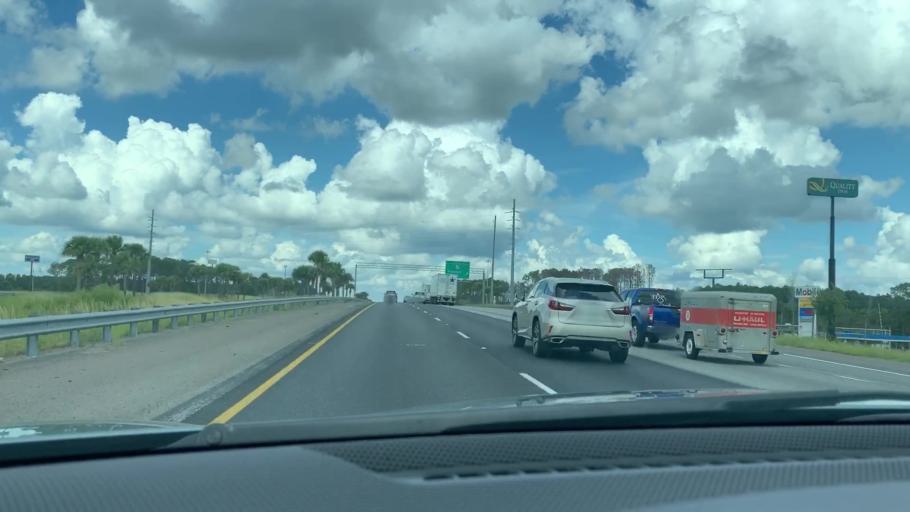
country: US
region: Georgia
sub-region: Camden County
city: Kingsland
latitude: 30.7883
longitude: -81.6580
